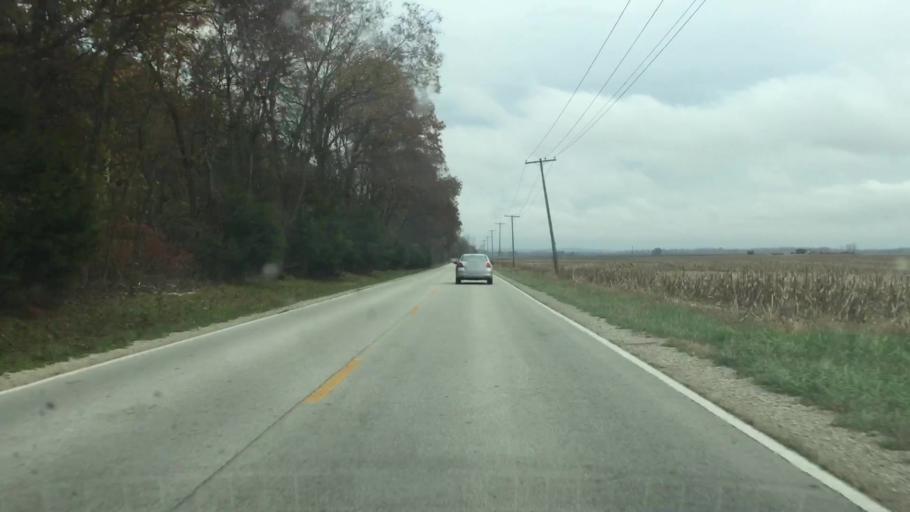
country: US
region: Missouri
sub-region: Gasconade County
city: Hermann
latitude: 38.7226
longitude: -91.4978
